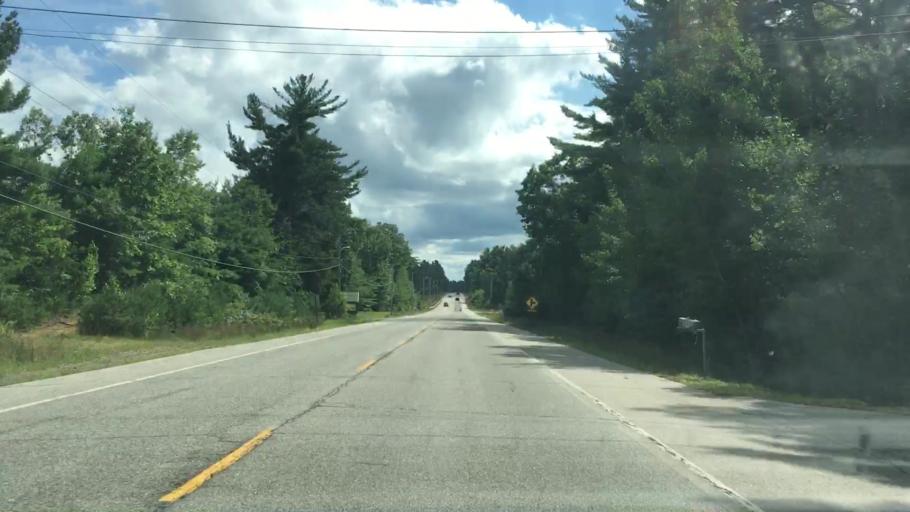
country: US
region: Maine
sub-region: York County
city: South Sanford
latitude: 43.3902
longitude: -70.7397
